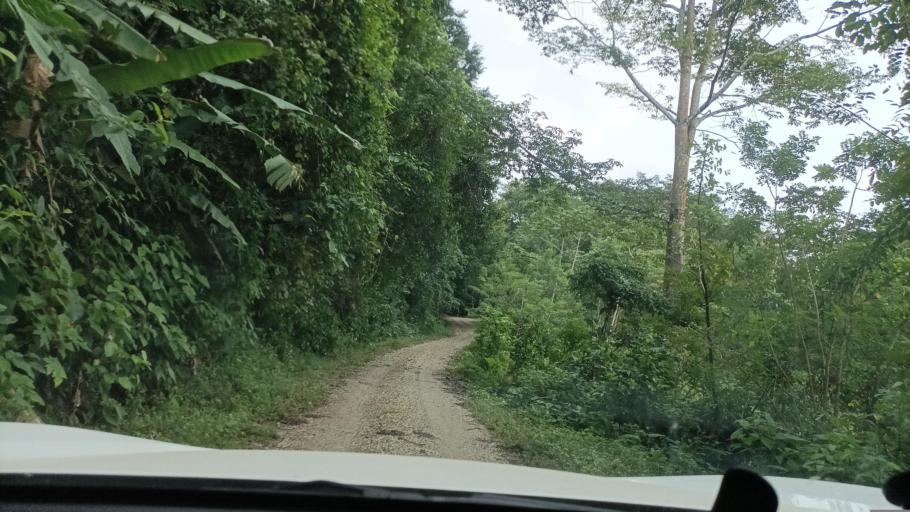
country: MX
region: Veracruz
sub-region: Uxpanapa
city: Poblado 10
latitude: 17.4402
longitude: -94.4096
